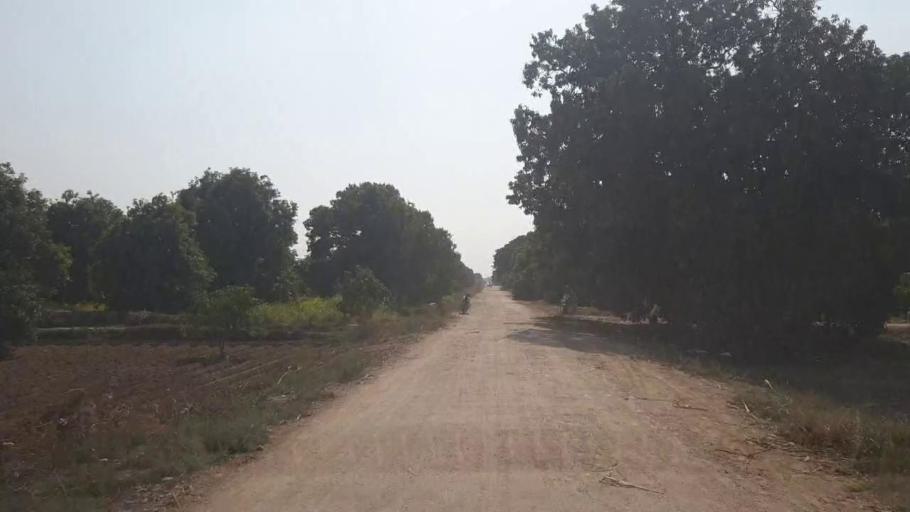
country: PK
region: Sindh
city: Tando Allahyar
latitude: 25.4863
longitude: 68.8351
